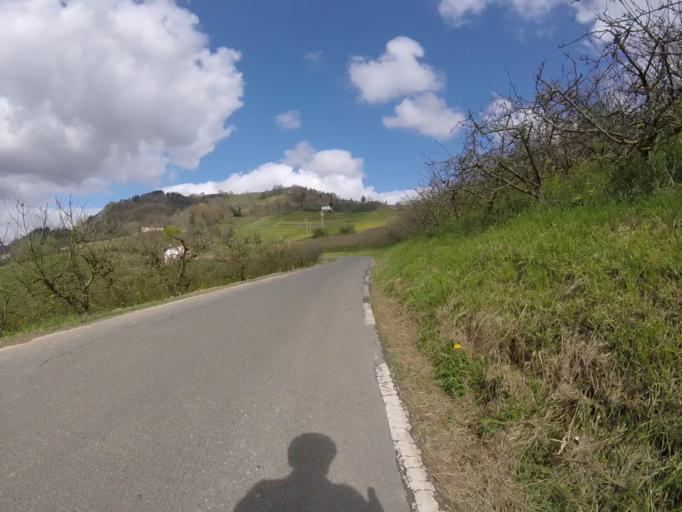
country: ES
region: Basque Country
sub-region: Provincia de Guipuzcoa
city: Tolosa
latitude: 43.1268
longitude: -2.0971
